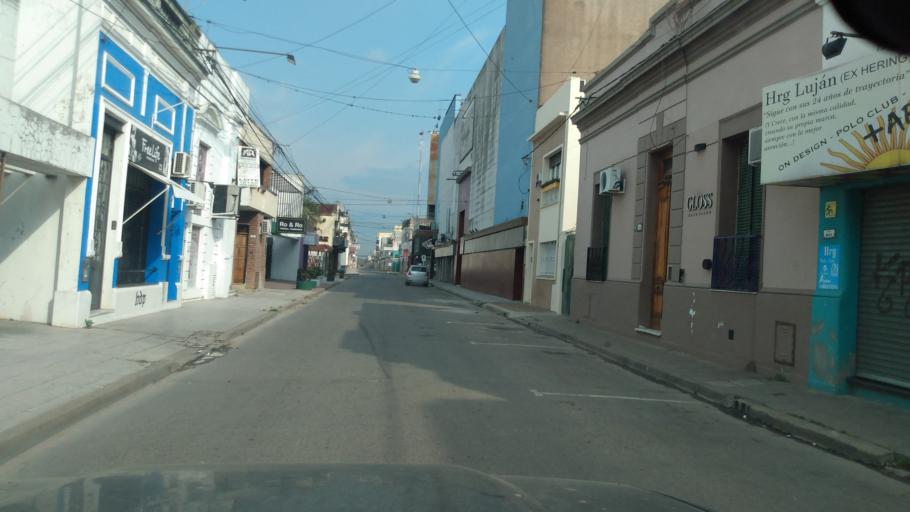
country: AR
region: Buenos Aires
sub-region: Partido de Lujan
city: Lujan
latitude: -34.5645
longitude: -59.1163
